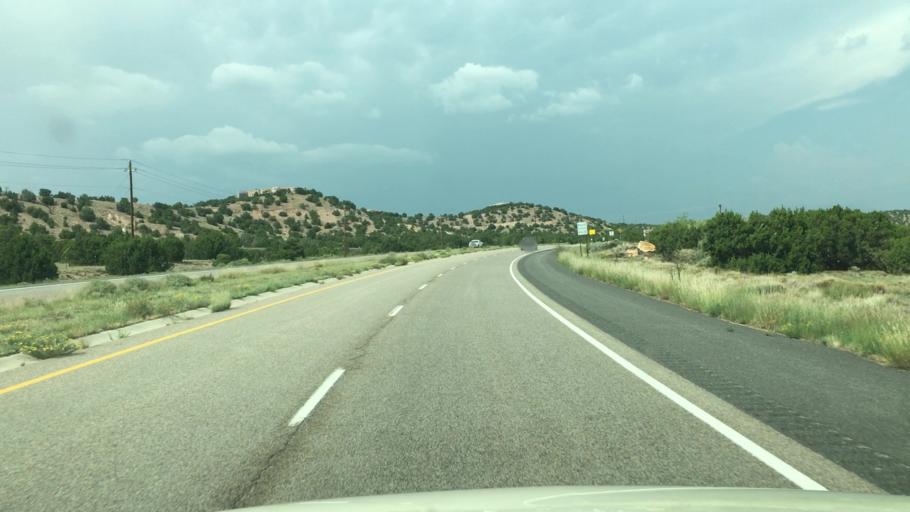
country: US
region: New Mexico
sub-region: Santa Fe County
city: Eldorado at Santa Fe
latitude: 35.4818
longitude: -105.9080
